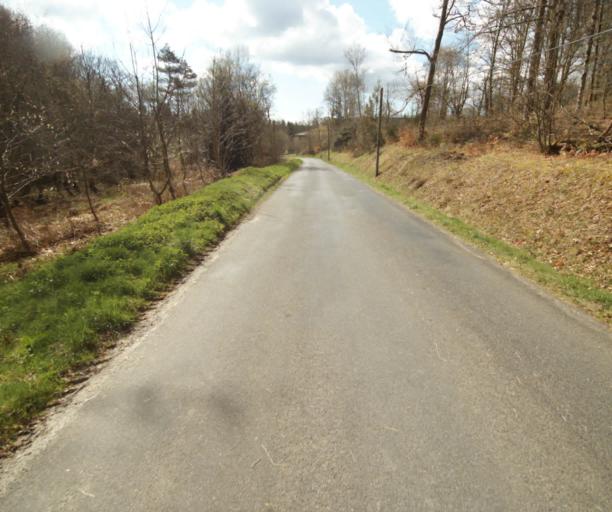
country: FR
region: Limousin
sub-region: Departement de la Correze
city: Correze
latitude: 45.2473
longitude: 1.9475
